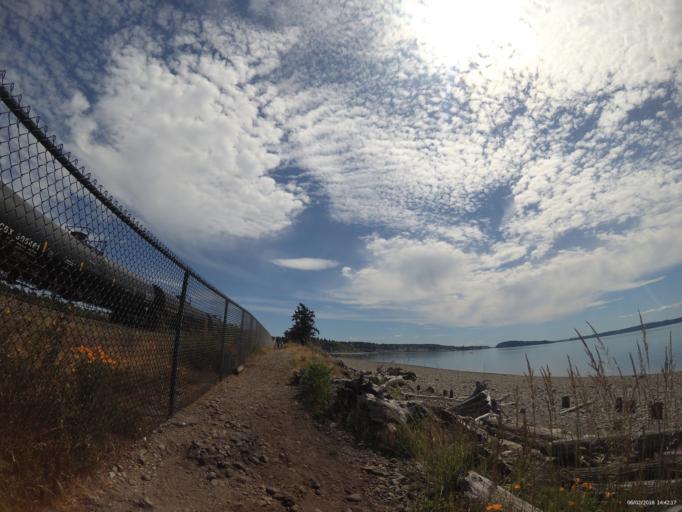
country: US
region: Washington
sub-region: Pierce County
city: Steilacoom
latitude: 47.1990
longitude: -122.5828
